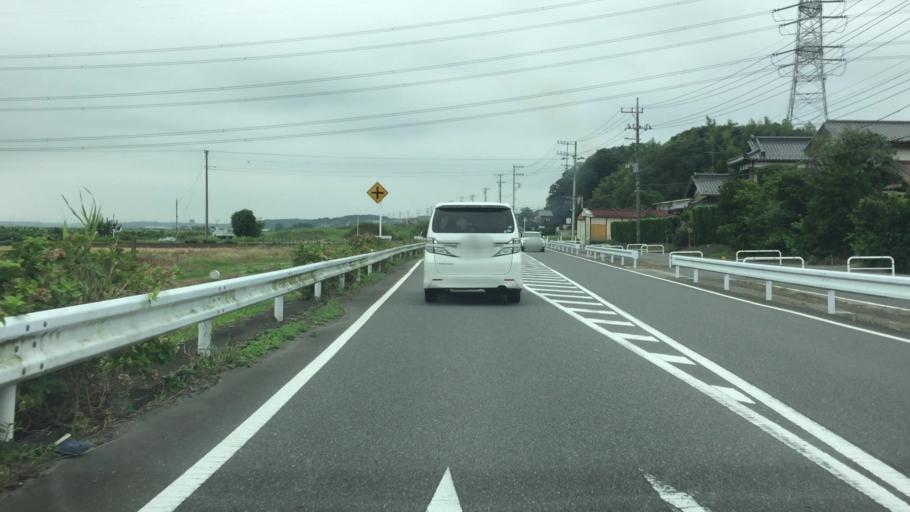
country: JP
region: Ibaraki
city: Toride
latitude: 35.8565
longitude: 140.1156
